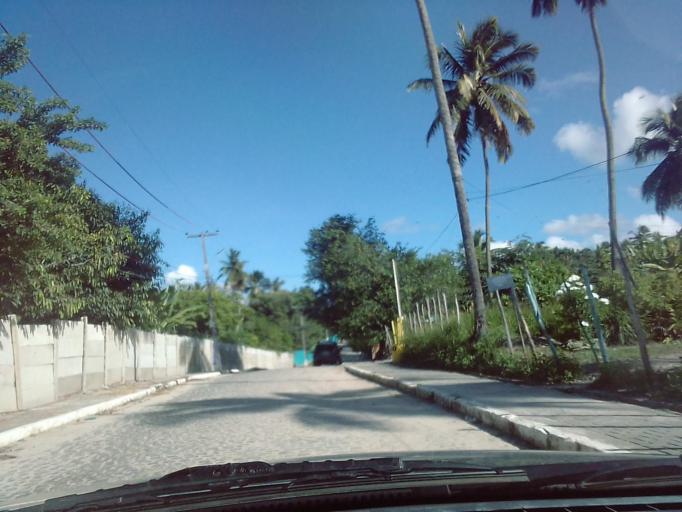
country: BR
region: Pernambuco
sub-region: Igarassu
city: Igarassu
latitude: -7.8404
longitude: -34.8459
